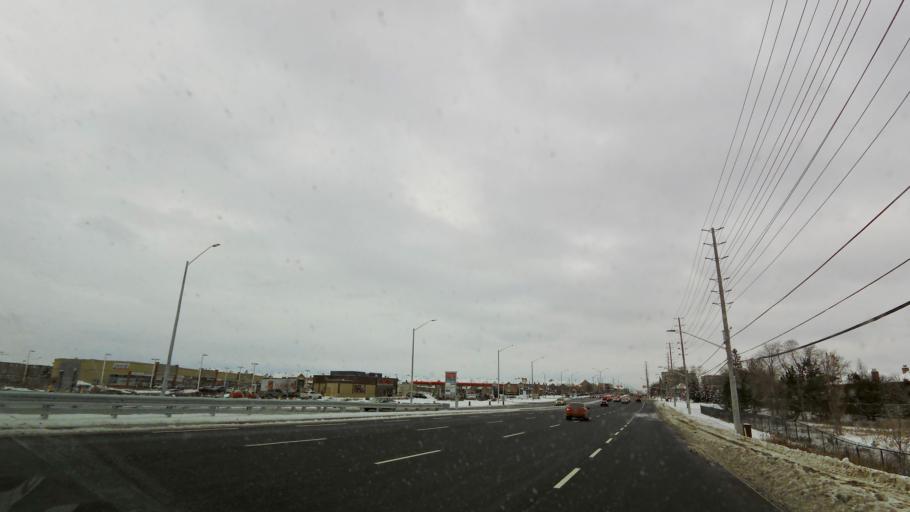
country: CA
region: Ontario
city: Mississauga
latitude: 43.5454
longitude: -79.7123
